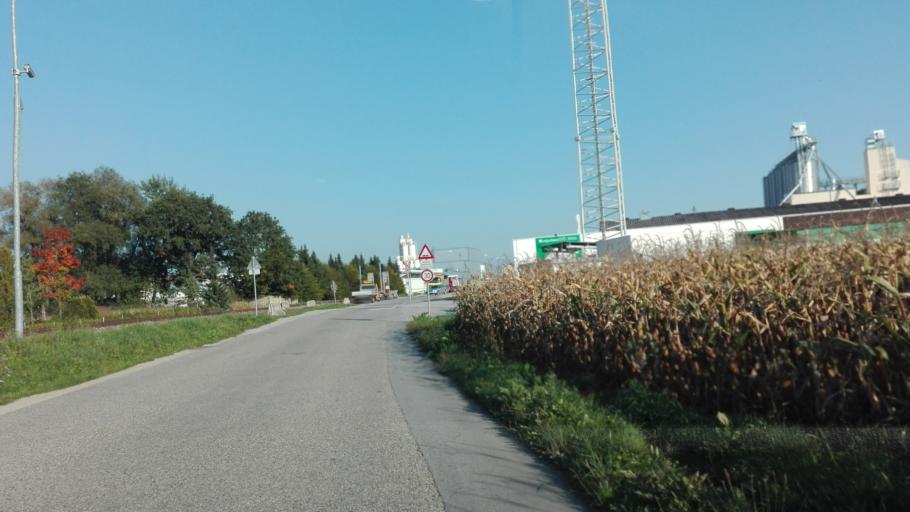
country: AT
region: Upper Austria
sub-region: Politischer Bezirk Perg
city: Perg
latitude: 48.2486
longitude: 14.6222
